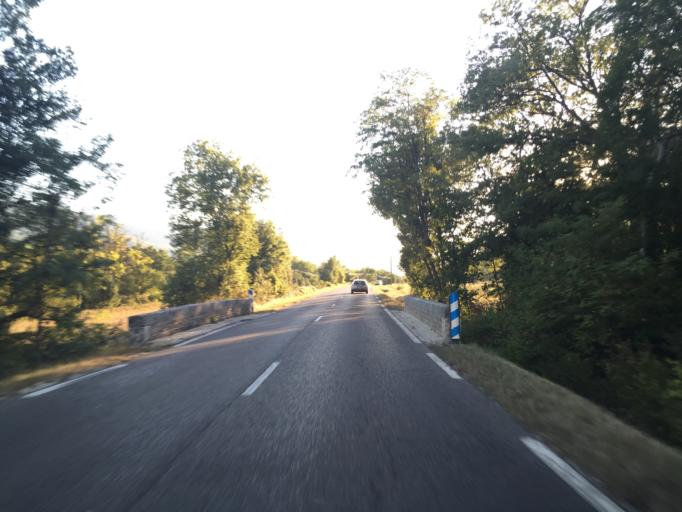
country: FR
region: Provence-Alpes-Cote d'Azur
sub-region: Departement des Alpes-de-Haute-Provence
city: Cereste
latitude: 43.8542
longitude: 5.5465
